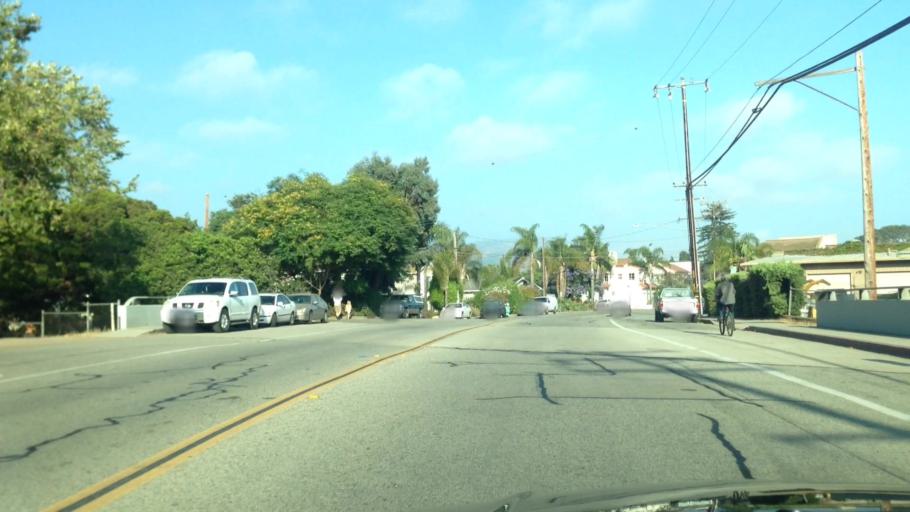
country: US
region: California
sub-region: Santa Barbara County
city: Carpinteria
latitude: 34.4014
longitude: -119.5220
